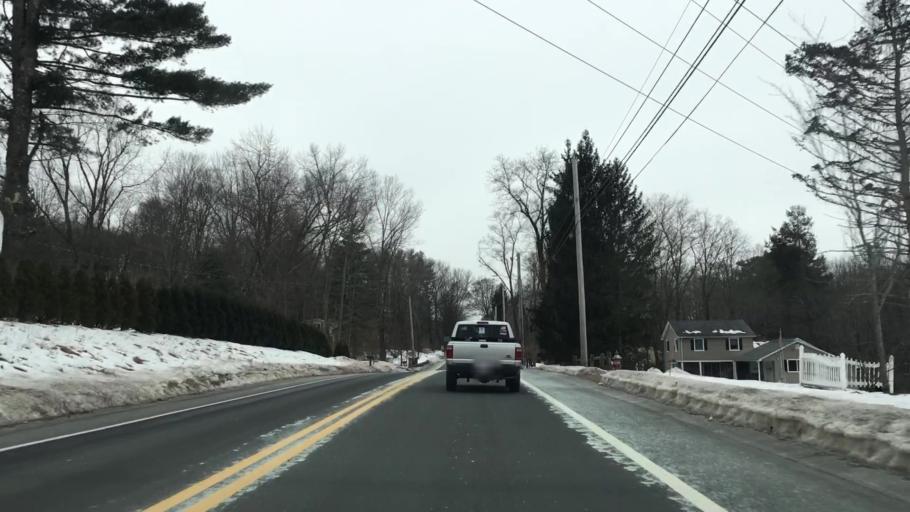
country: US
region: Massachusetts
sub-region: Hampden County
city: Westfield
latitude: 42.1028
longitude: -72.7061
